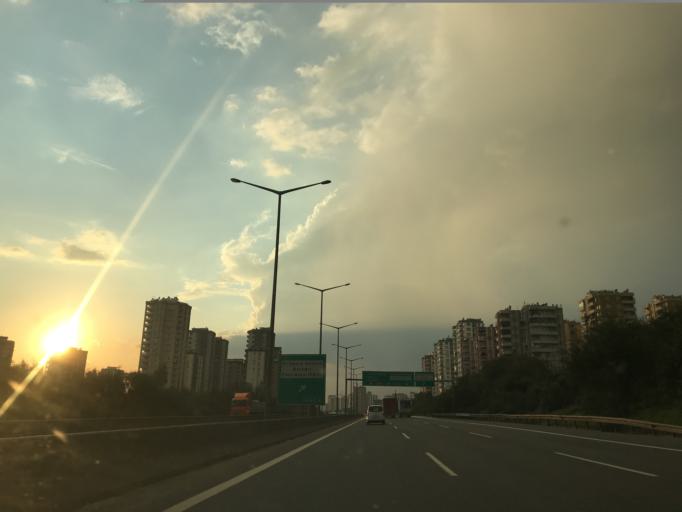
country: TR
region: Adana
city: Seyhan
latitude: 37.0314
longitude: 35.2634
